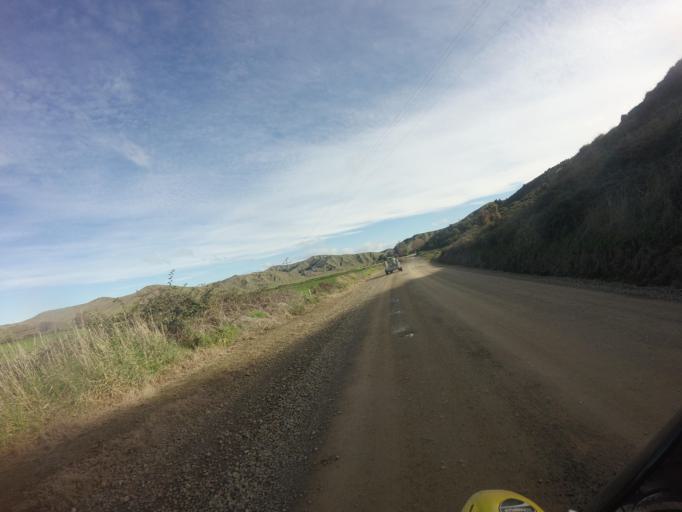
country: NZ
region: Hawke's Bay
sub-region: Wairoa District
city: Wairoa
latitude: -39.0288
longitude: 177.5862
